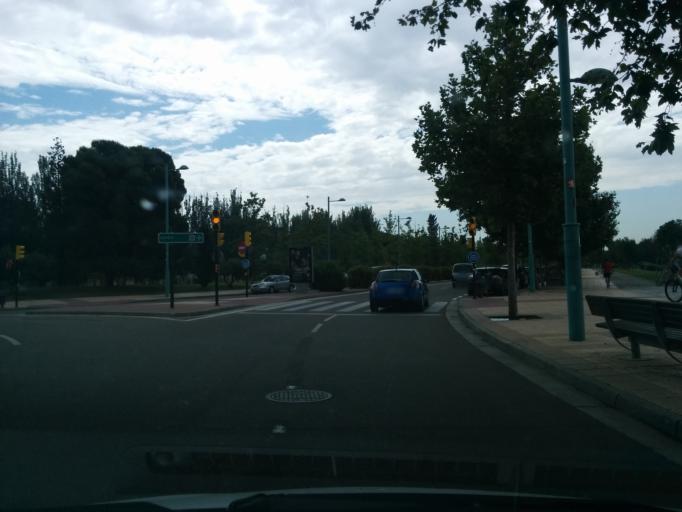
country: ES
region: Aragon
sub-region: Provincia de Zaragoza
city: Almozara
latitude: 41.6665
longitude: -0.8948
